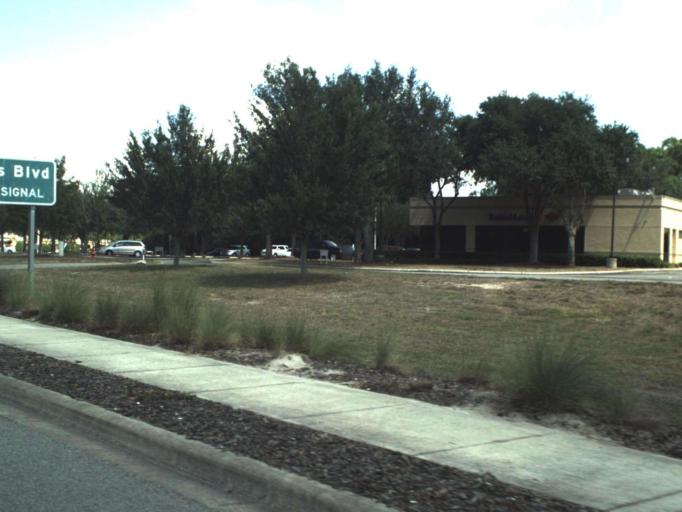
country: US
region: Florida
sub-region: Lake County
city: Silver Lake
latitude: 28.8204
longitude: -81.7785
